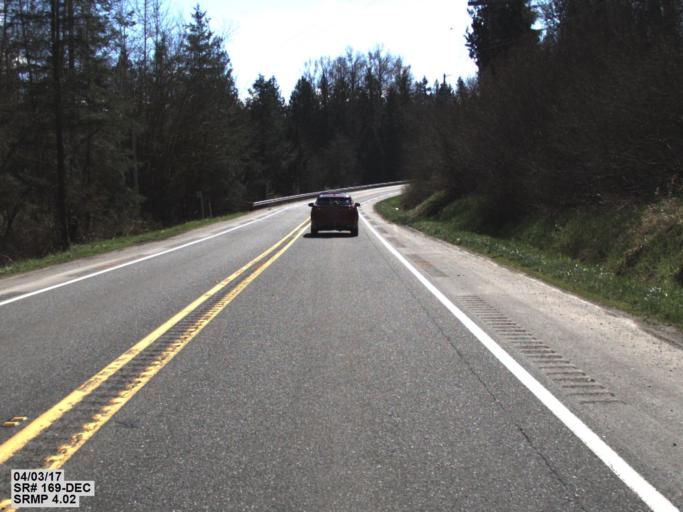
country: US
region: Washington
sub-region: King County
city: Black Diamond
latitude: 47.2617
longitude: -121.9856
